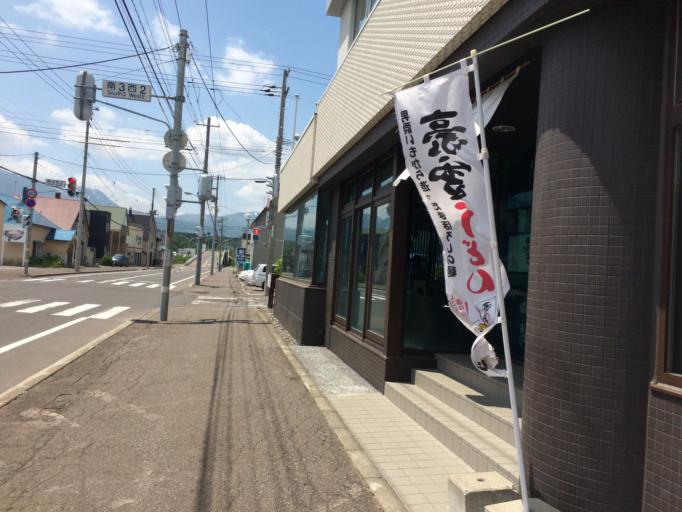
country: JP
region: Hokkaido
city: Niseko Town
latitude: 42.8992
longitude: 140.7494
